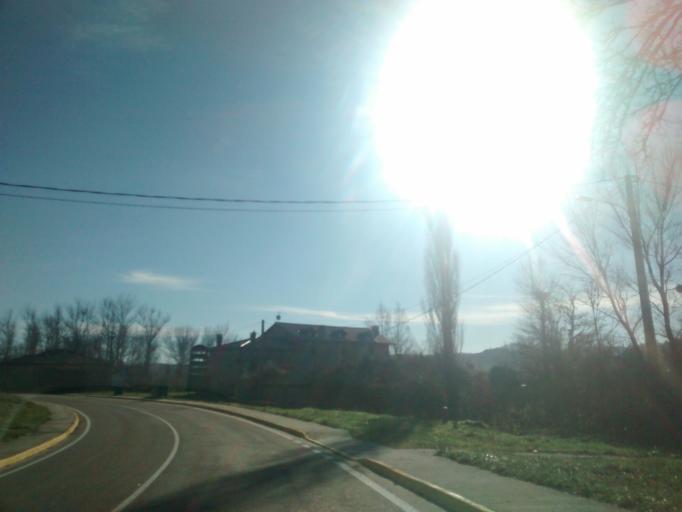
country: ES
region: Castille and Leon
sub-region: Provincia de Burgos
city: Arija
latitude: 42.9827
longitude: -3.8140
